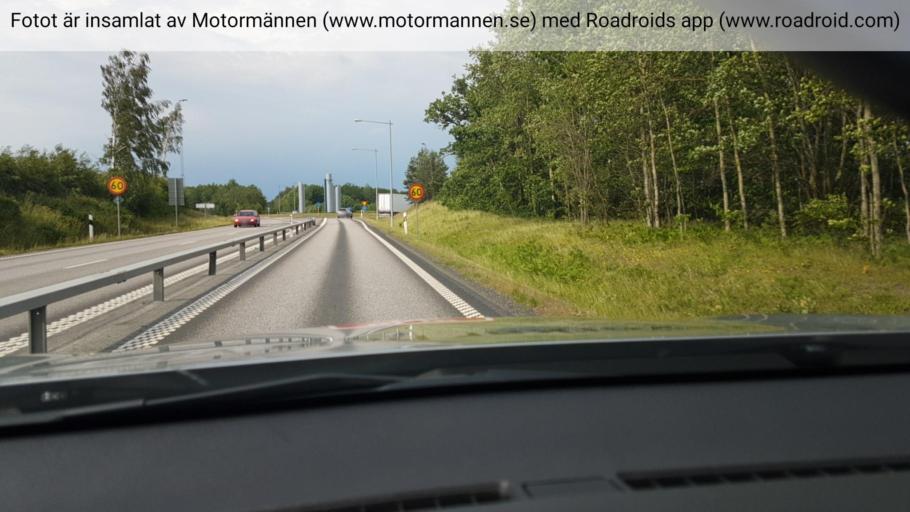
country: SE
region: Joenkoeping
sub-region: Habo Kommun
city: Habo
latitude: 57.8973
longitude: 14.1056
